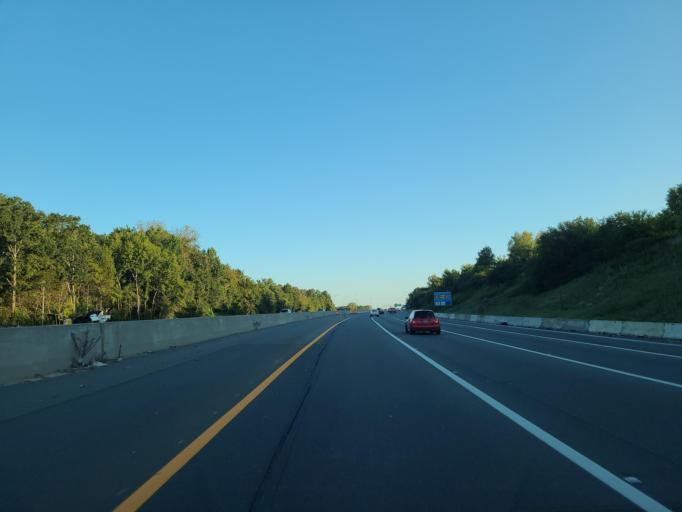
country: US
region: North Carolina
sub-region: Mecklenburg County
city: Pineville
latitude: 35.0772
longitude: -80.8720
